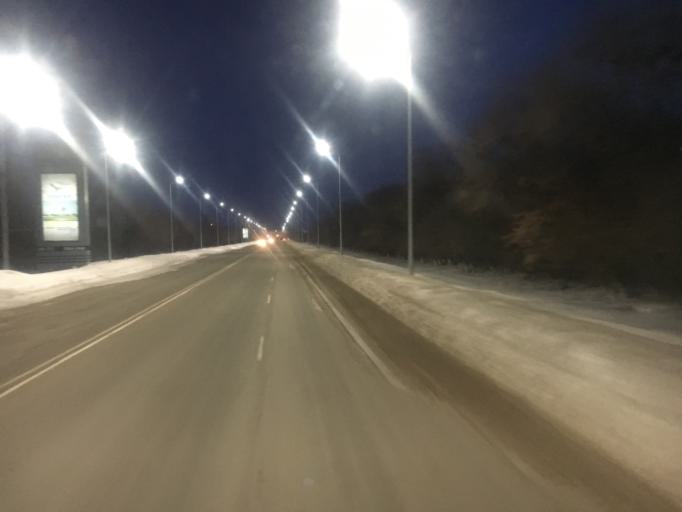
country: KZ
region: Batys Qazaqstan
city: Oral
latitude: 51.1584
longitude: 51.5324
